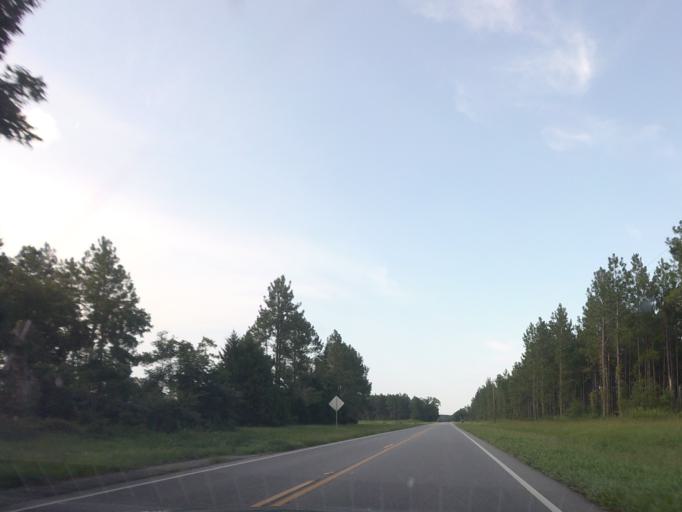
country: US
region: Georgia
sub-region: Bleckley County
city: Cochran
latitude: 32.4347
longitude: -83.3040
